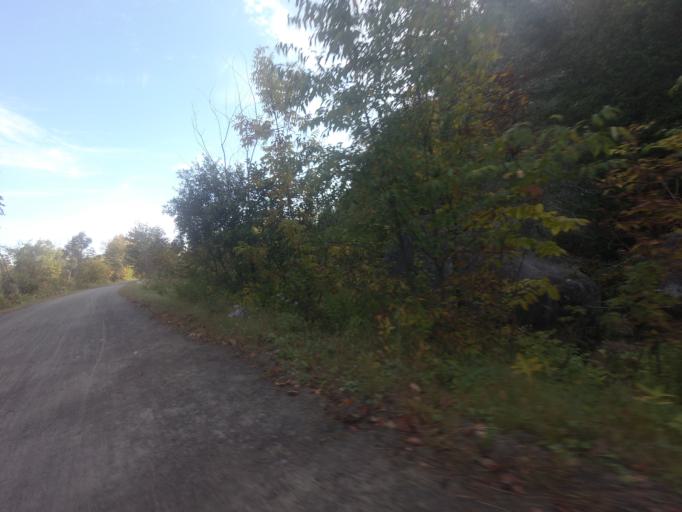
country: CA
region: Quebec
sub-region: Laurentides
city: Sainte-Adele
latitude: 45.9508
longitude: -74.1133
